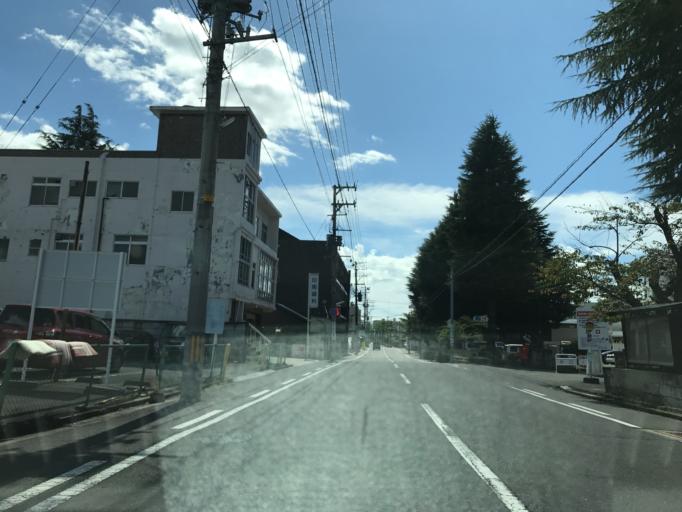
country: JP
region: Fukushima
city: Koriyama
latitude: 37.3967
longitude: 140.3774
